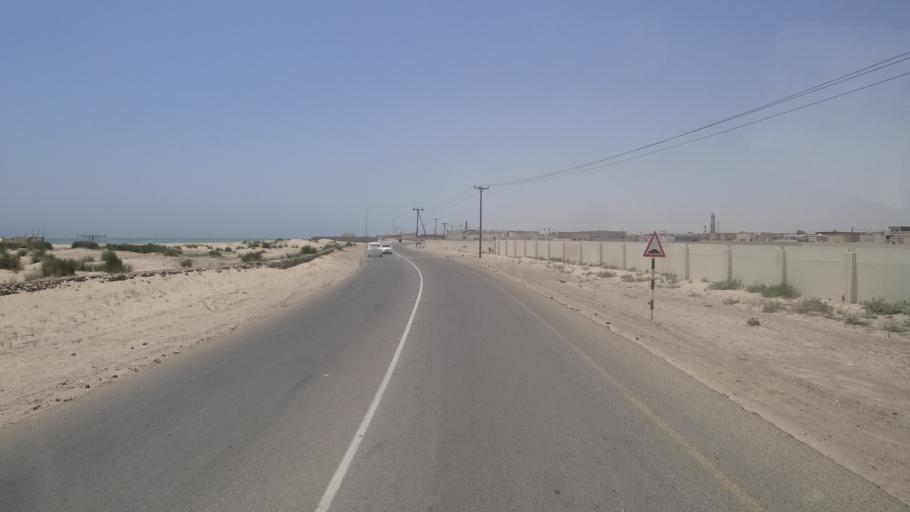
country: OM
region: Ash Sharqiyah
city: Sur
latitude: 22.0893
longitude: 59.6897
